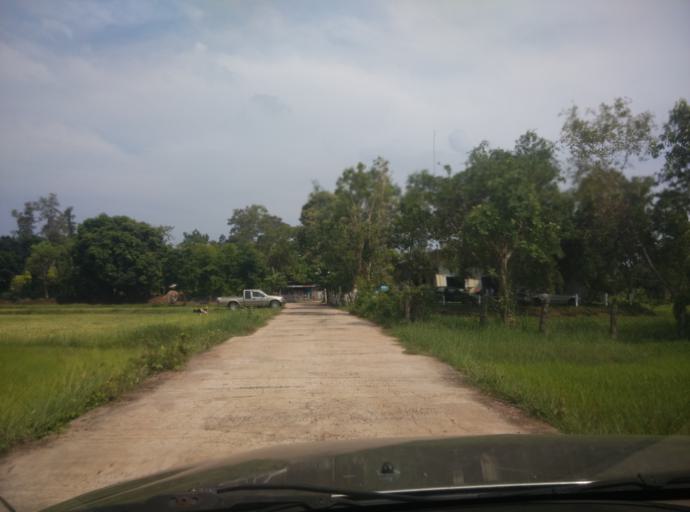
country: TH
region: Sisaket
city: Huai Thap Than
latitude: 15.0503
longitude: 104.0855
